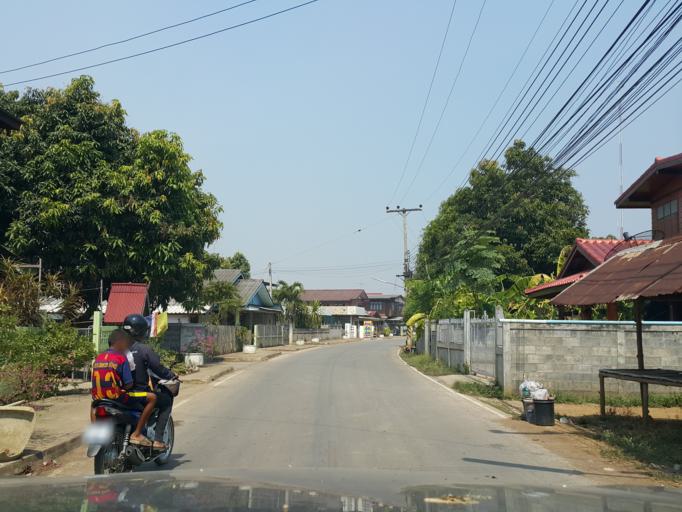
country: TH
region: Sukhothai
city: Thung Saliam
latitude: 17.3120
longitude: 99.5506
